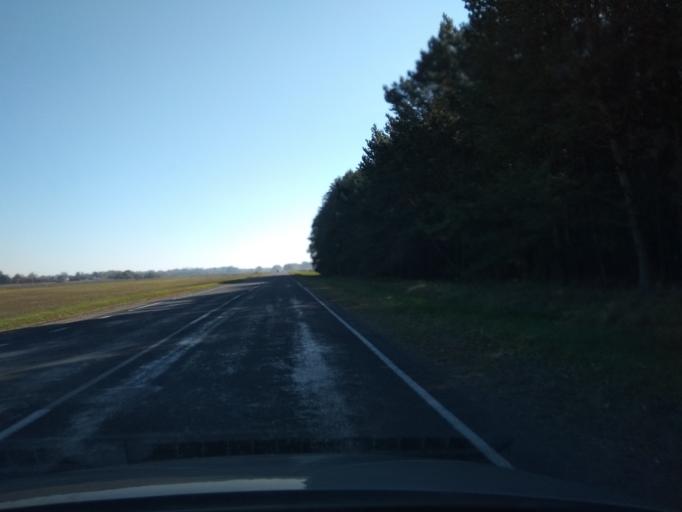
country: BY
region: Brest
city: Malaryta
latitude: 51.9445
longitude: 24.0245
